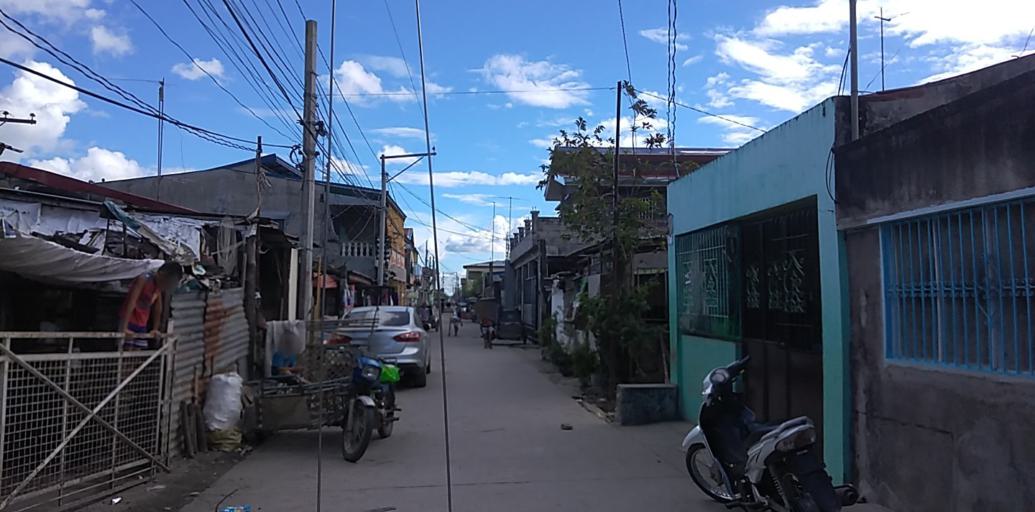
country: PH
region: Central Luzon
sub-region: Province of Pampanga
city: Arayat
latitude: 15.1407
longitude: 120.7692
